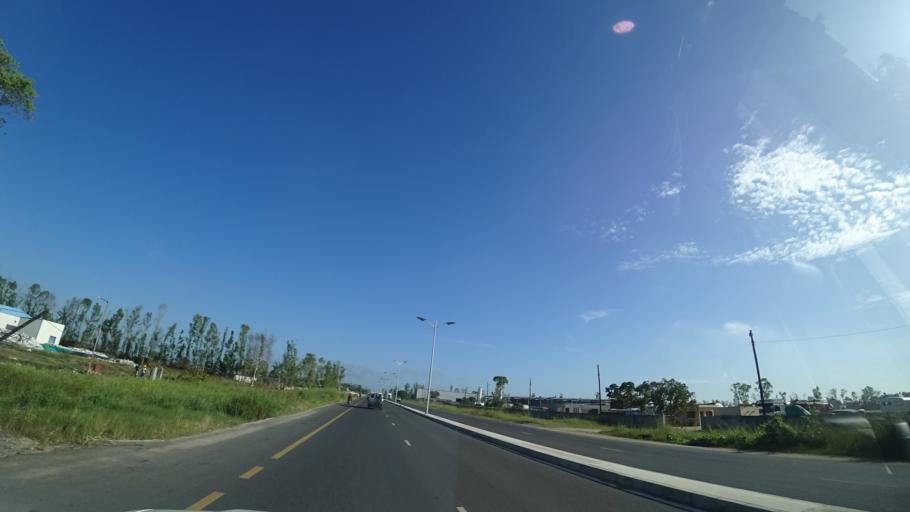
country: MZ
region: Sofala
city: Dondo
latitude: -19.7072
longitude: 34.7928
